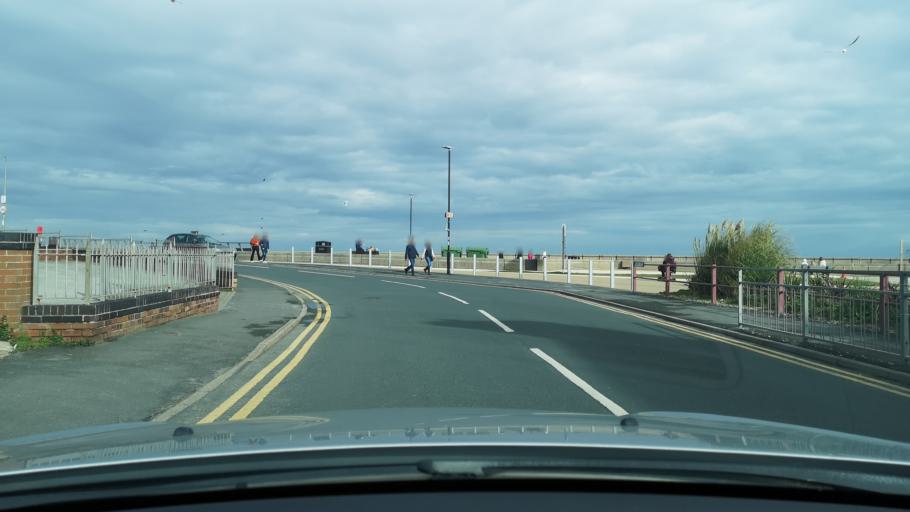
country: GB
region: England
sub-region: East Riding of Yorkshire
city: Hornsea
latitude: 53.9134
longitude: -0.1616
